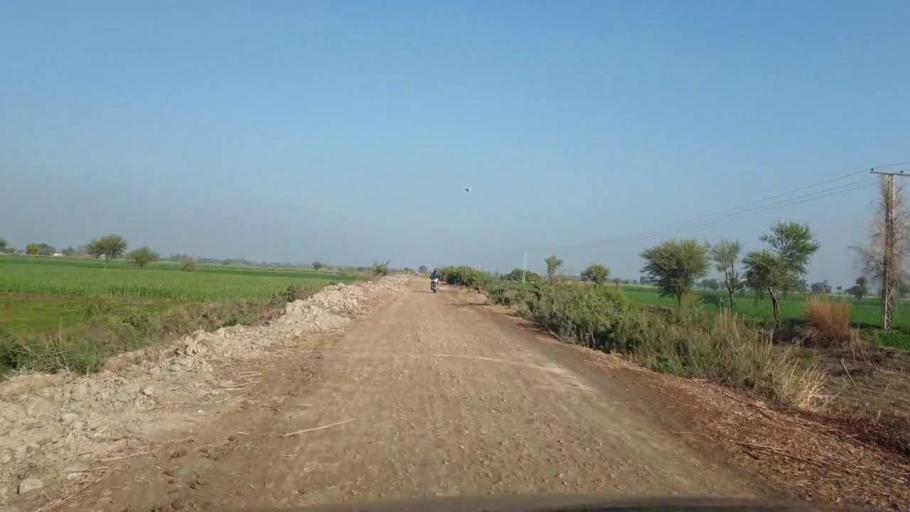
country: PK
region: Sindh
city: Sinjhoro
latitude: 26.0467
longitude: 68.7886
